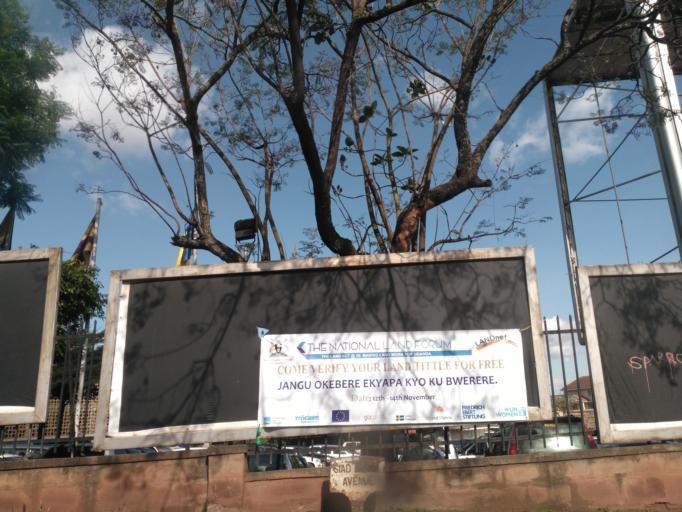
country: UG
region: Central Region
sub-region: Kampala District
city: Kampala
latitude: 0.3155
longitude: 32.5885
